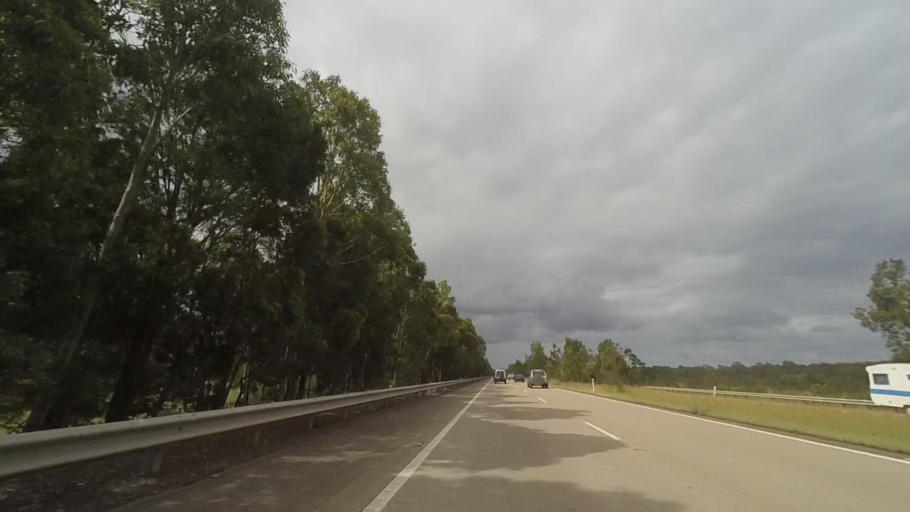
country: AU
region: New South Wales
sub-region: Port Stephens Shire
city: Raymond Terrace
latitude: -32.7298
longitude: 151.7836
